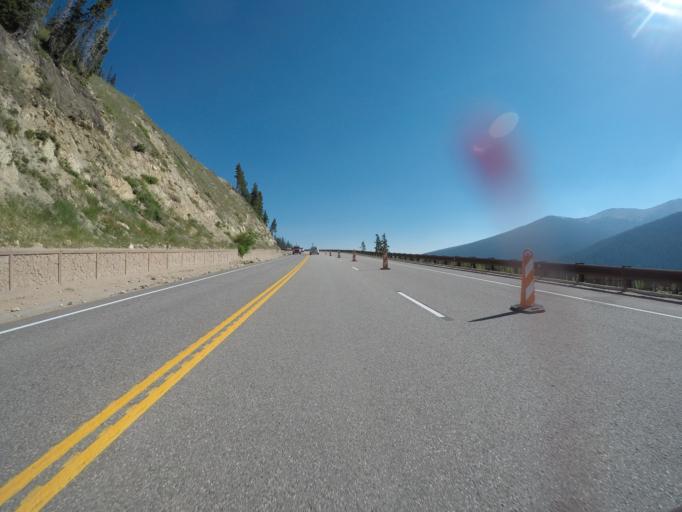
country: US
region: Colorado
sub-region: Grand County
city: Fraser
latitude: 39.8419
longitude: -105.7568
